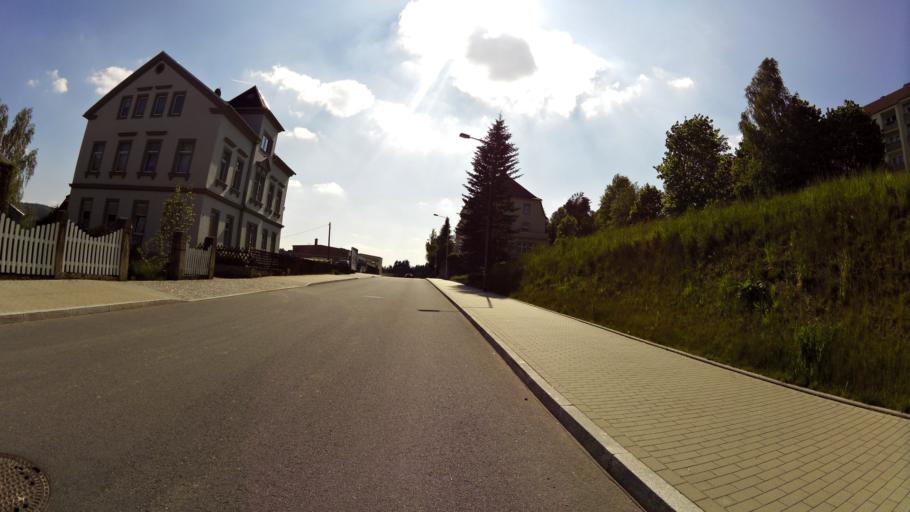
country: DE
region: Saxony
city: Sebnitz
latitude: 50.9765
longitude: 14.2699
